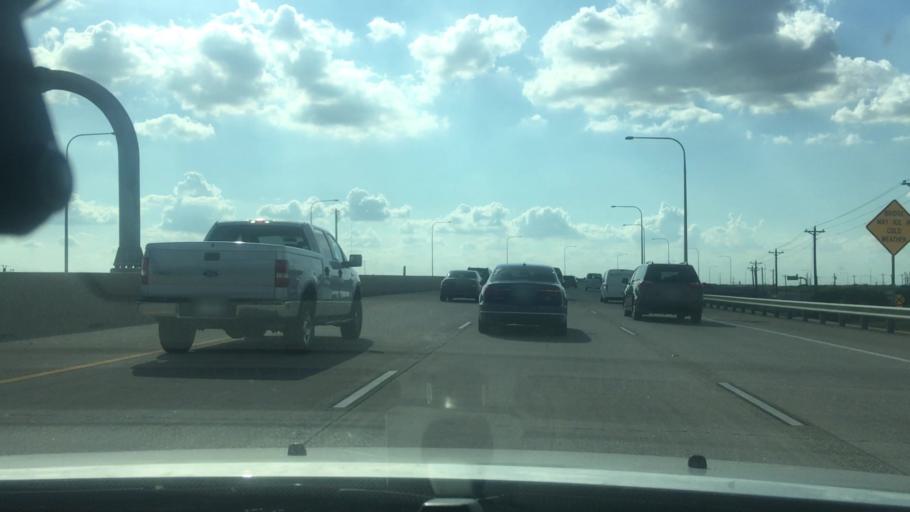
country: US
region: Texas
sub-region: Collin County
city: Frisco
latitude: 33.1363
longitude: -96.8331
